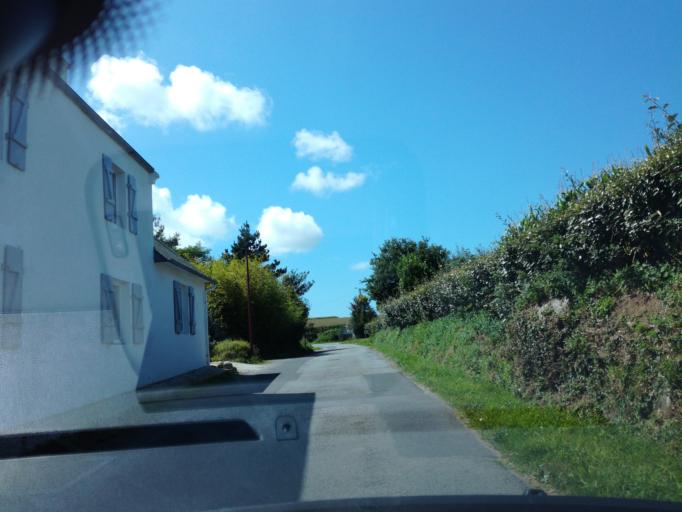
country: FR
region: Brittany
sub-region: Departement du Finistere
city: Saint-Pabu
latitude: 48.5622
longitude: -4.5996
